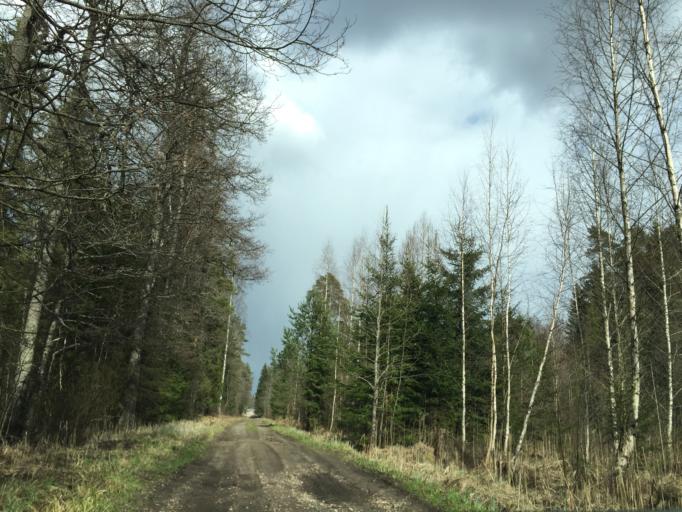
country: LV
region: Garkalne
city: Garkalne
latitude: 56.9642
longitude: 24.4844
